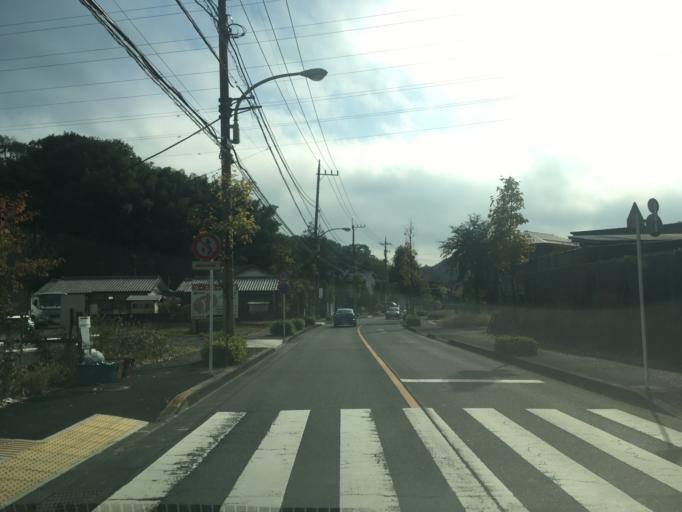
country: JP
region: Tokyo
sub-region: Machida-shi
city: Machida
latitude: 35.6012
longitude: 139.4212
